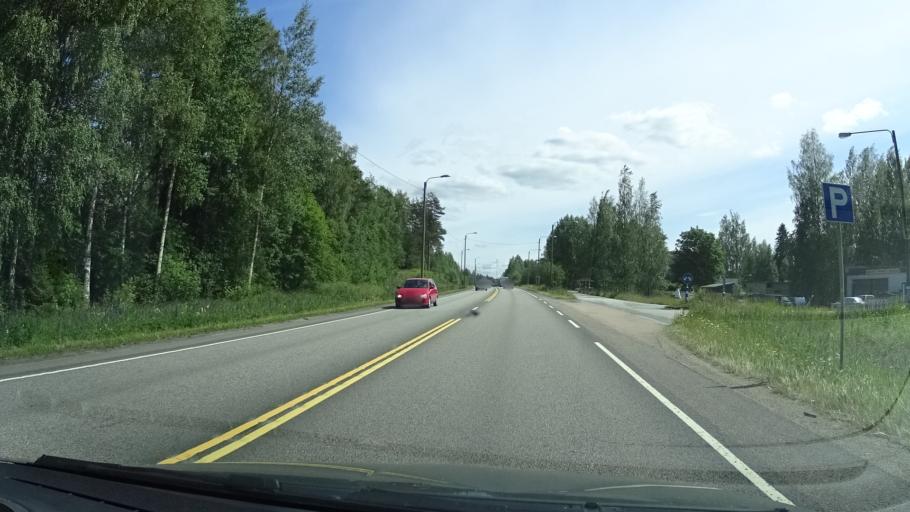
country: FI
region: Central Finland
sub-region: Jyvaeskylae
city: Uurainen
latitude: 62.2660
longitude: 25.4470
